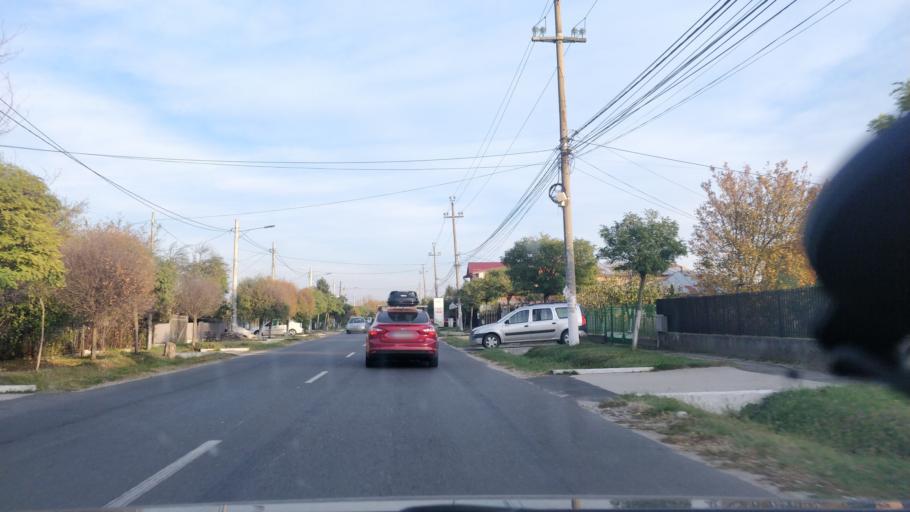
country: RO
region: Ilfov
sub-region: Comuna Ciorogarla
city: Ciorogarla
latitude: 44.4441
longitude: 25.8684
